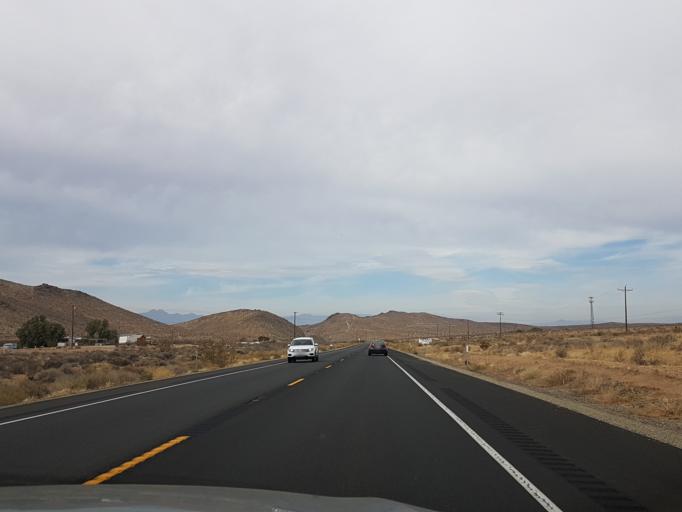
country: US
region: California
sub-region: Kern County
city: Ridgecrest
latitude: 35.5328
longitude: -117.6813
